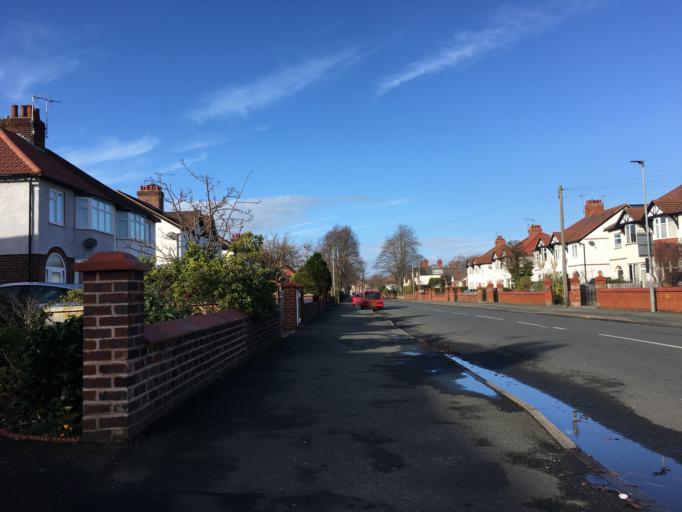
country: GB
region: England
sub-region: Cheshire West and Chester
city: Hoole
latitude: 53.1996
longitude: -2.8668
